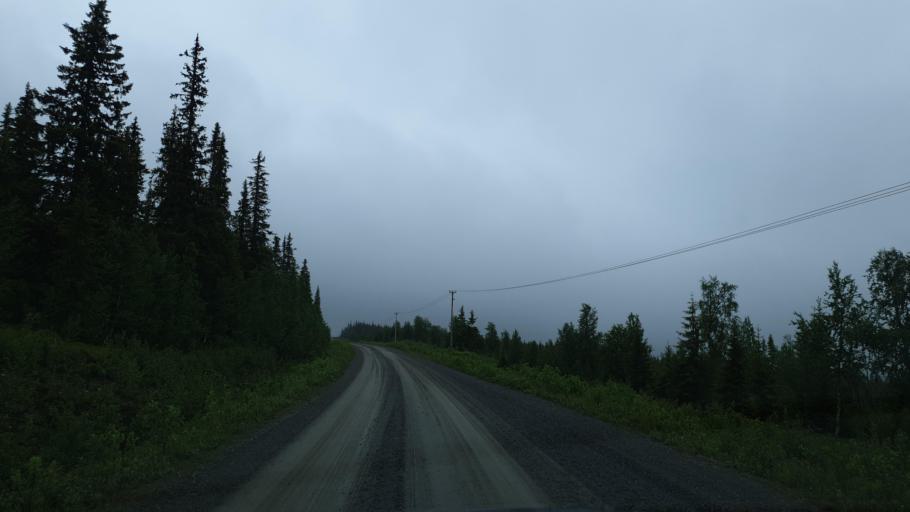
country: SE
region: Vaesterbotten
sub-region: Vilhelmina Kommun
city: Sjoberg
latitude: 65.3226
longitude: 15.9338
